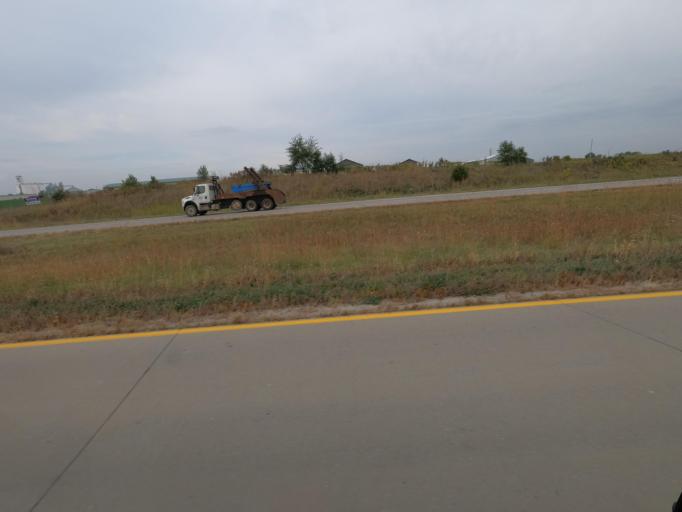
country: US
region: Iowa
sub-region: Marion County
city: Pella
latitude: 41.3901
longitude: -92.8964
